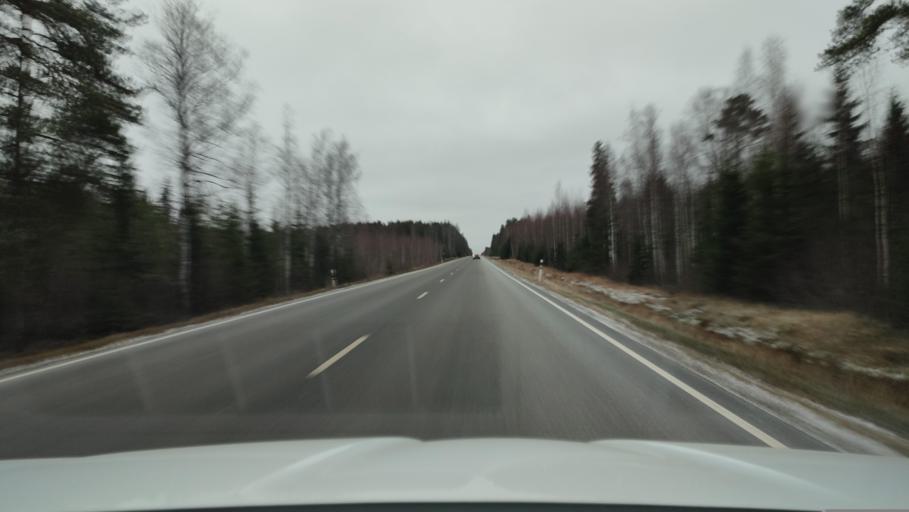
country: FI
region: Ostrobothnia
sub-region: Sydosterbotten
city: Naerpes
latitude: 62.5665
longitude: 21.4838
